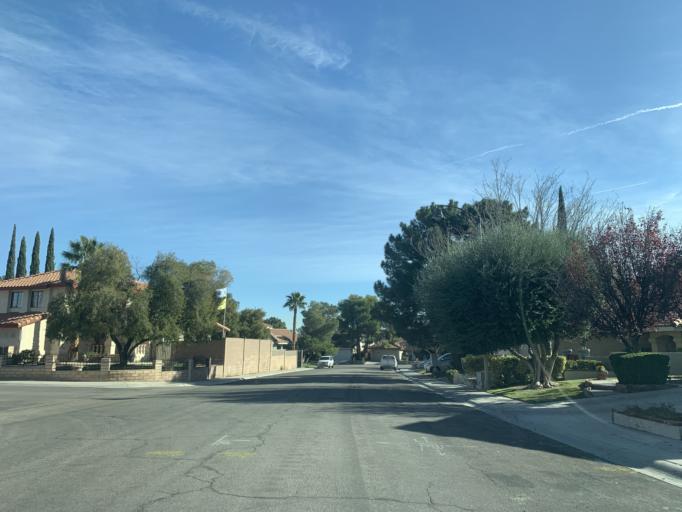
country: US
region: Nevada
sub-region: Clark County
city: Summerlin South
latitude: 36.1358
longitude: -115.2918
